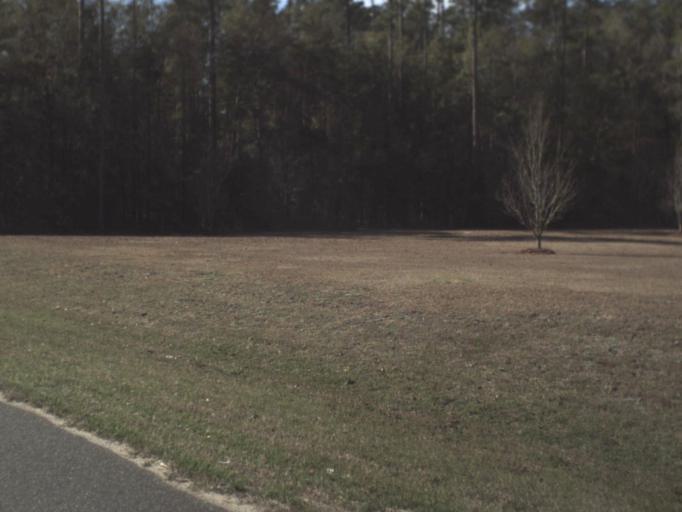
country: US
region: Florida
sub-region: Jackson County
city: Malone
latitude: 30.9241
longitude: -85.1614
